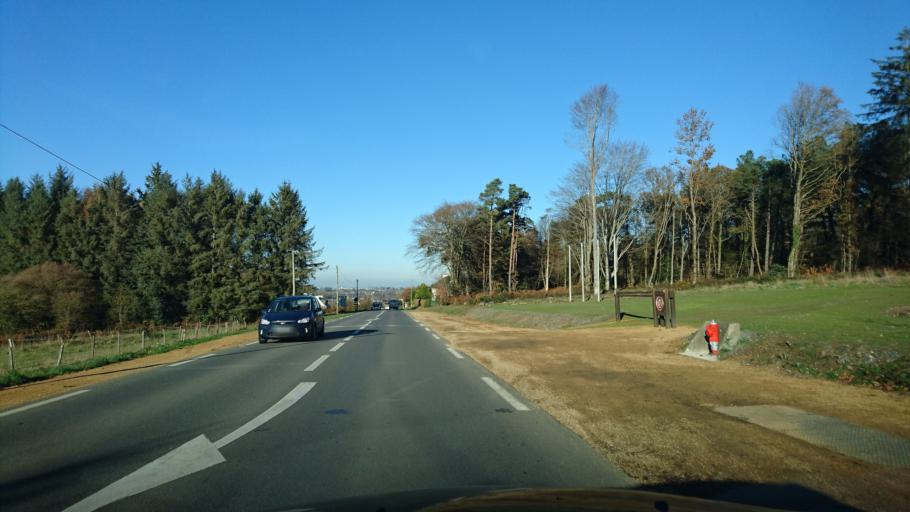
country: FR
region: Brittany
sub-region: Departement des Cotes-d'Armor
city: Pledran
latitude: 48.4518
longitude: -2.7524
